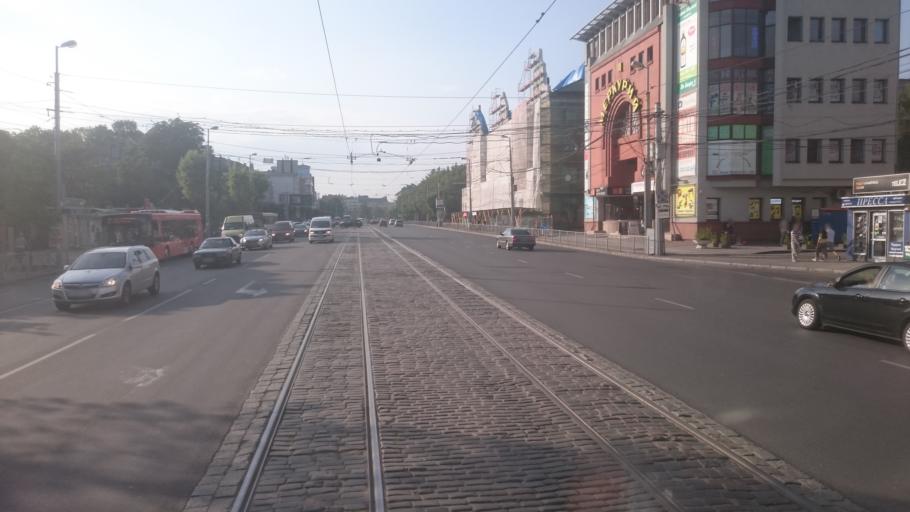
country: RU
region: Kaliningrad
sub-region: Gorod Kaliningrad
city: Kaliningrad
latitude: 54.7124
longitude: 20.5081
